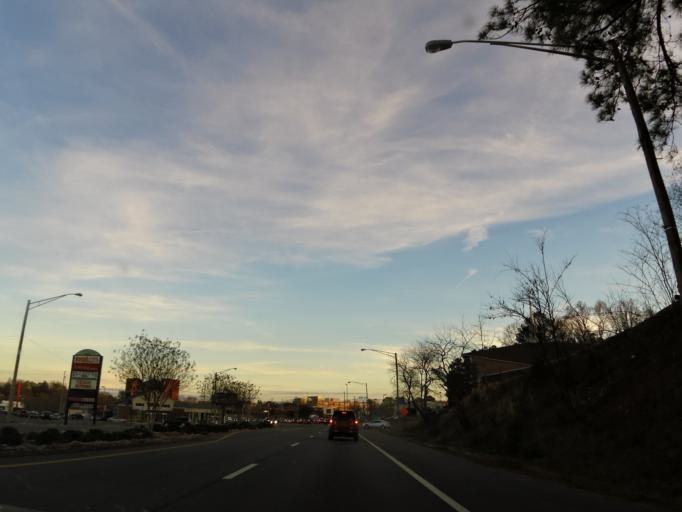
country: US
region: Tennessee
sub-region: Bradley County
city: Cleveland
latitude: 35.1844
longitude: -84.8749
